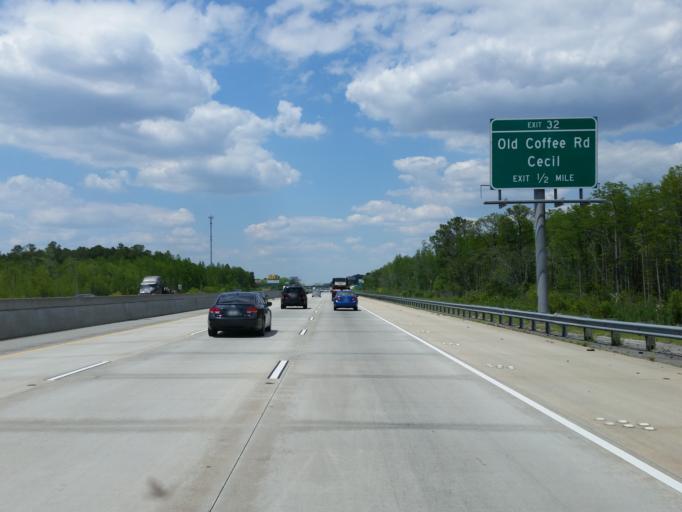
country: US
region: Georgia
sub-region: Lowndes County
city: Hahira
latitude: 31.0333
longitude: -83.3980
